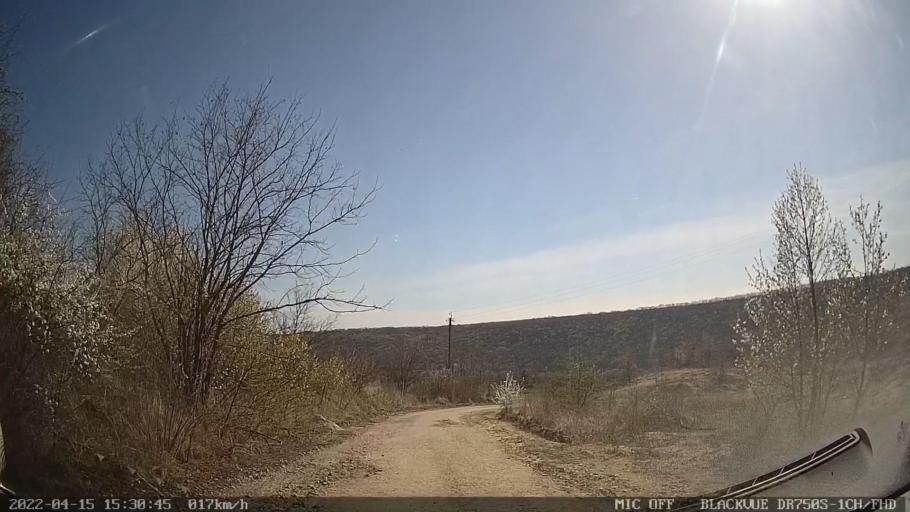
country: MD
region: Raionul Ocnita
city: Otaci
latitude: 48.3540
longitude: 27.9228
